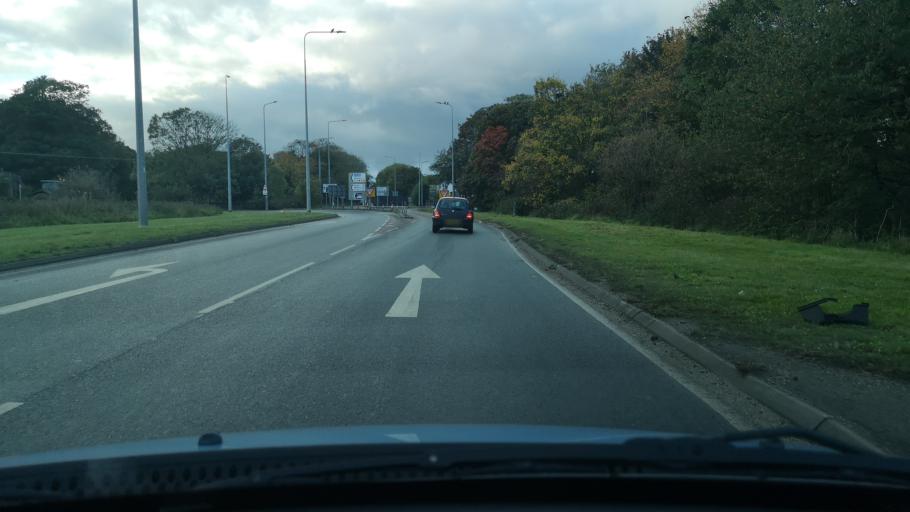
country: GB
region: England
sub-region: North Lincolnshire
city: Crowle
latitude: 53.5854
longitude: -0.8179
